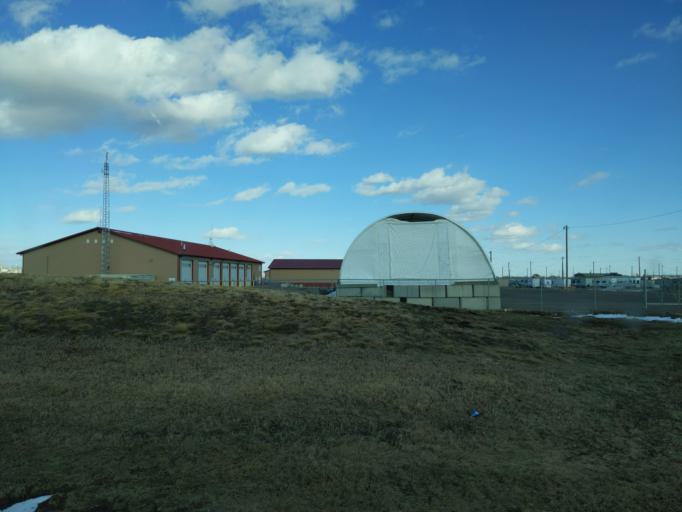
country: CA
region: Saskatchewan
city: Lloydminster
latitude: 53.2478
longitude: -109.9791
